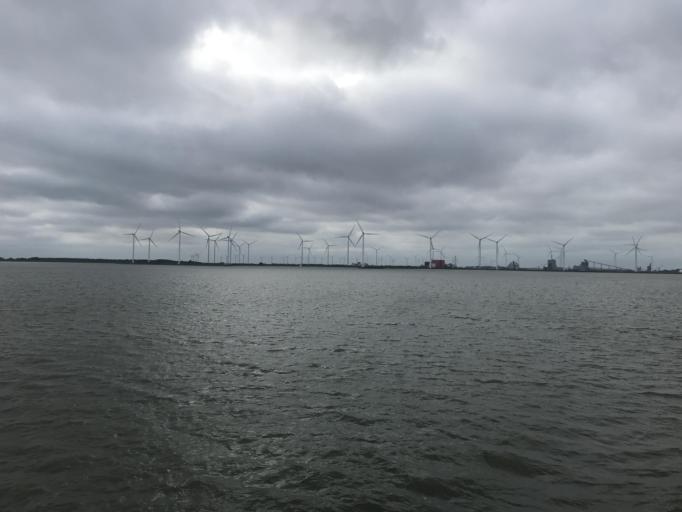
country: NL
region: Groningen
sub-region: Gemeente Delfzijl
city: Delfzijl
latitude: 53.3286
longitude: 7.0184
